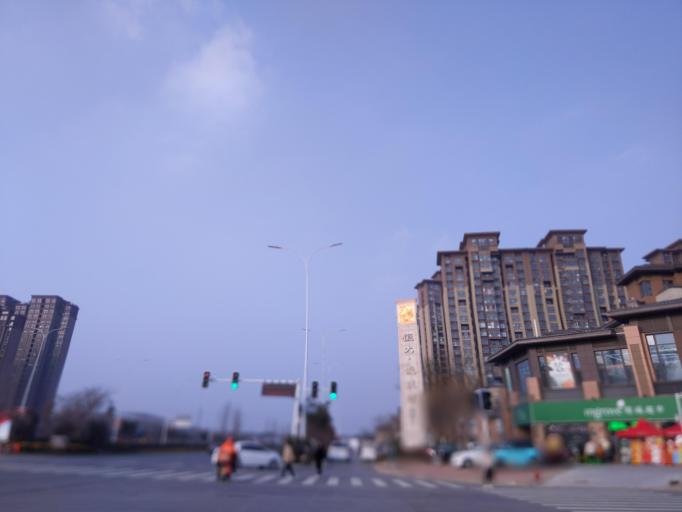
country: CN
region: Henan Sheng
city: Puyang
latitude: 35.8137
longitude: 115.0226
